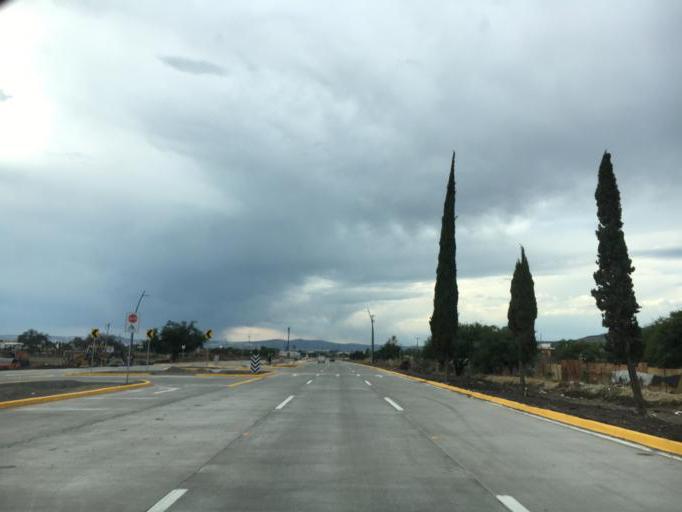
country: MX
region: Guanajuato
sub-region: Leon
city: Fraccionamiento Paraiso Real
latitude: 21.1094
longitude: -101.5838
